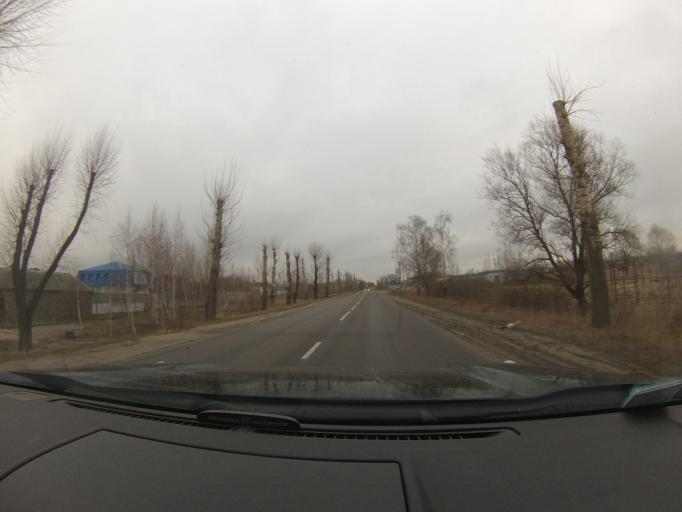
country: RU
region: Moskovskaya
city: Lopatinskiy
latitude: 55.3327
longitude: 38.7255
